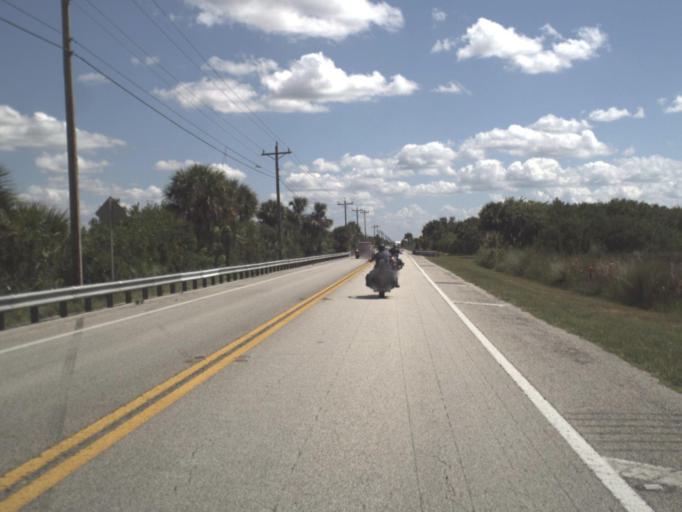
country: US
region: Florida
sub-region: Collier County
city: Marco
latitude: 25.9587
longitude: -81.4918
